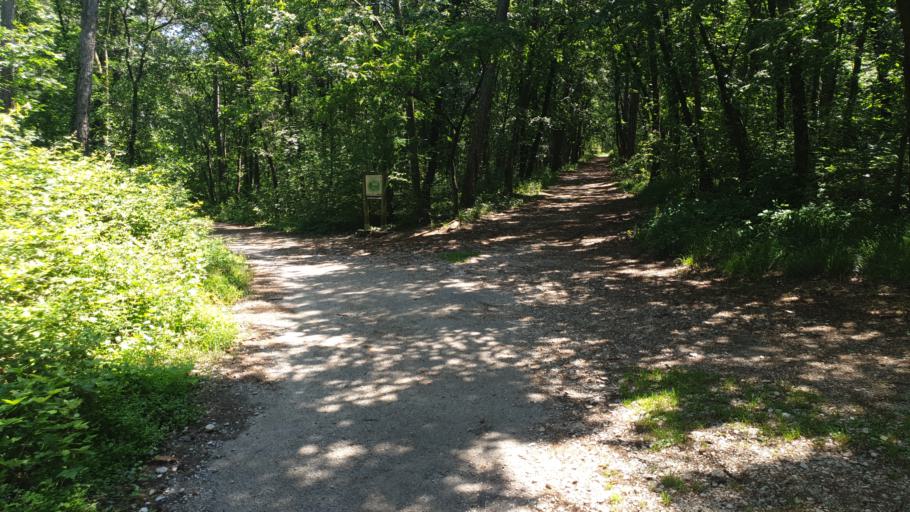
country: IT
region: Friuli Venezia Giulia
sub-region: Provincia di Trieste
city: Villa Opicina
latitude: 45.6889
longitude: 13.7663
